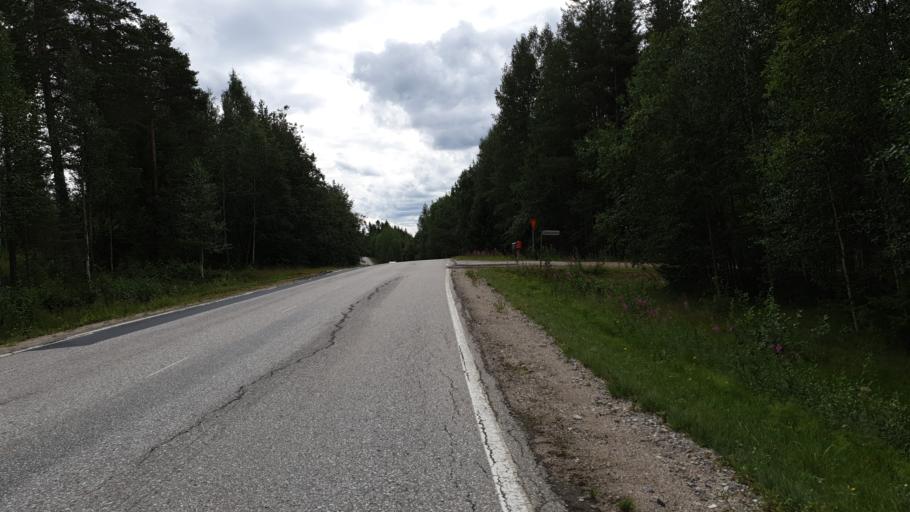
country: FI
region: Kainuu
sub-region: Kehys-Kainuu
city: Kuhmo
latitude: 64.4570
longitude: 29.7691
